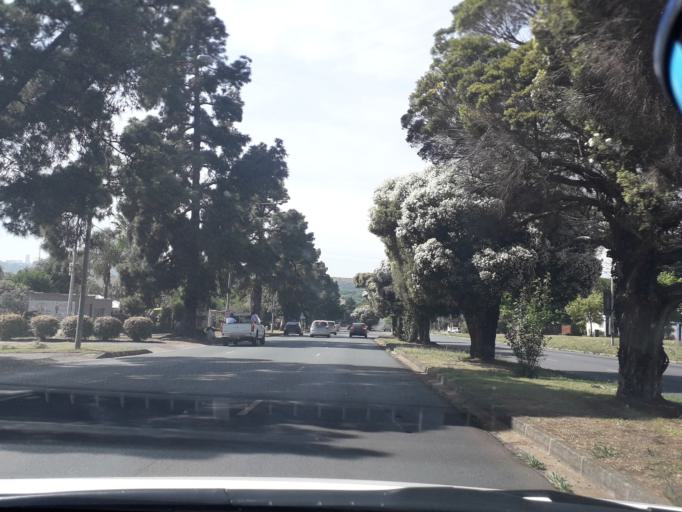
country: ZA
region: Gauteng
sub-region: City of Johannesburg Metropolitan Municipality
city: Johannesburg
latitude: -26.1480
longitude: 27.9865
